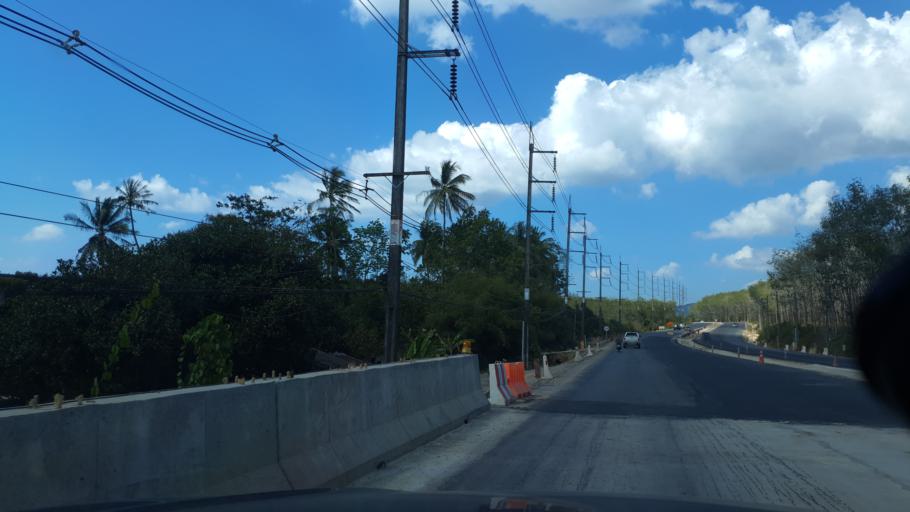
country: TH
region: Phangnga
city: Ban Khao Lak
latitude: 8.5520
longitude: 98.2709
